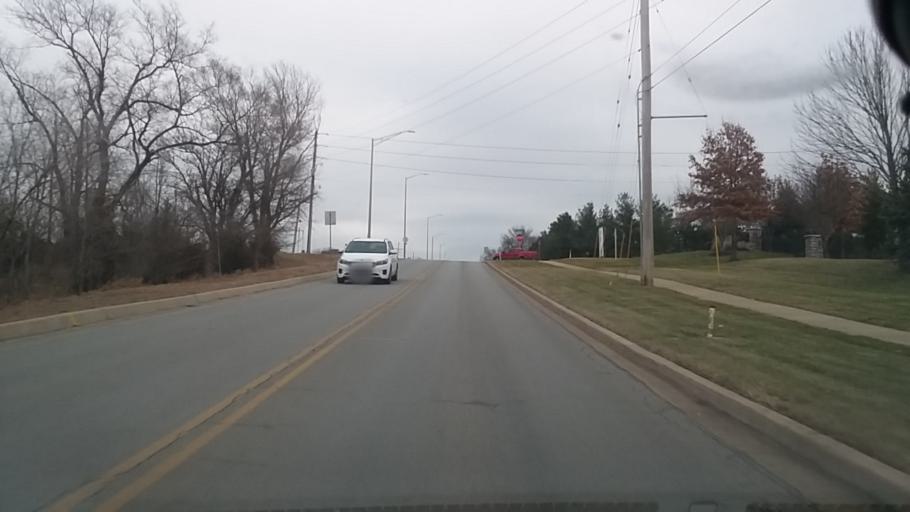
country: US
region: Kansas
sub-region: Johnson County
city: Olathe
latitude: 38.9127
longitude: -94.8355
